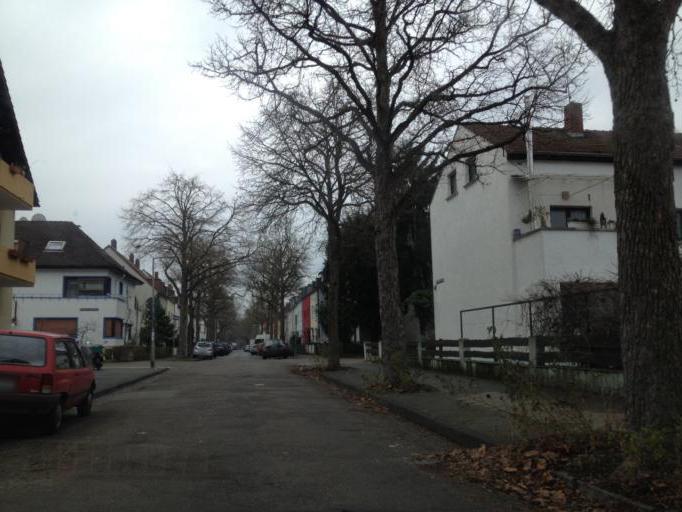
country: DE
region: Rheinland-Pfalz
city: Altrip
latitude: 49.4640
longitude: 8.4828
